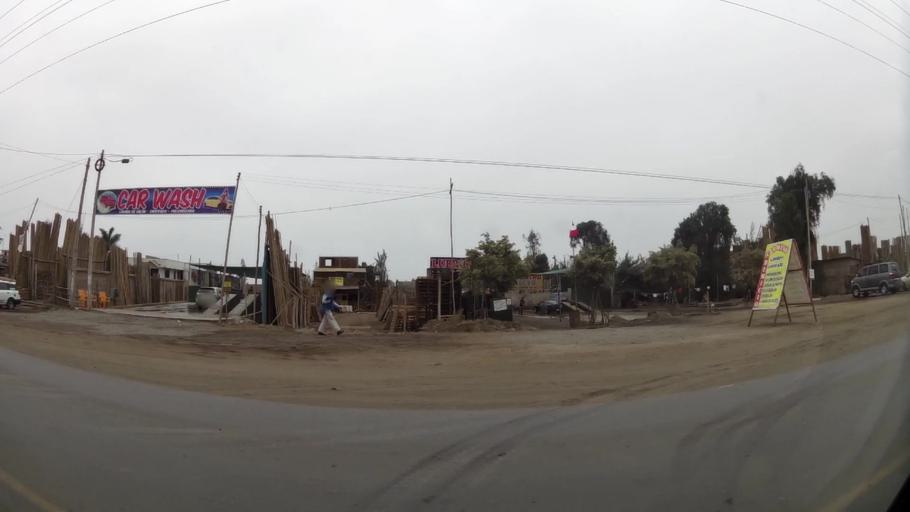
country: PE
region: Lima
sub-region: Lima
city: Punta Hermosa
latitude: -12.2682
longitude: -76.8776
